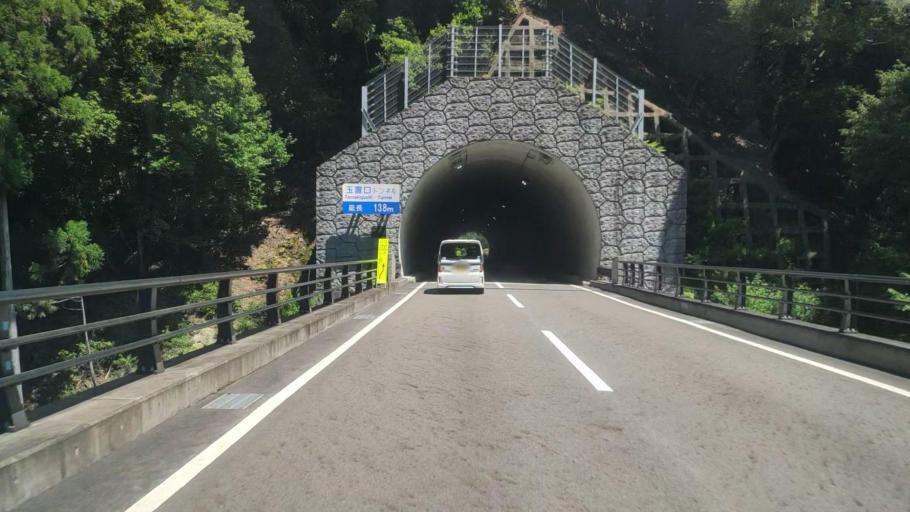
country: JP
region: Wakayama
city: Shingu
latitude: 33.8894
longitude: 135.8798
